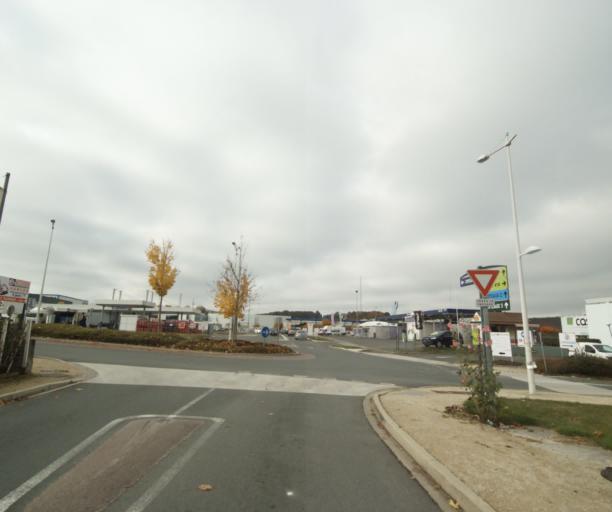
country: FR
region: Poitou-Charentes
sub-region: Departement de la Charente-Maritime
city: Saintes
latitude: 45.7470
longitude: -0.6737
